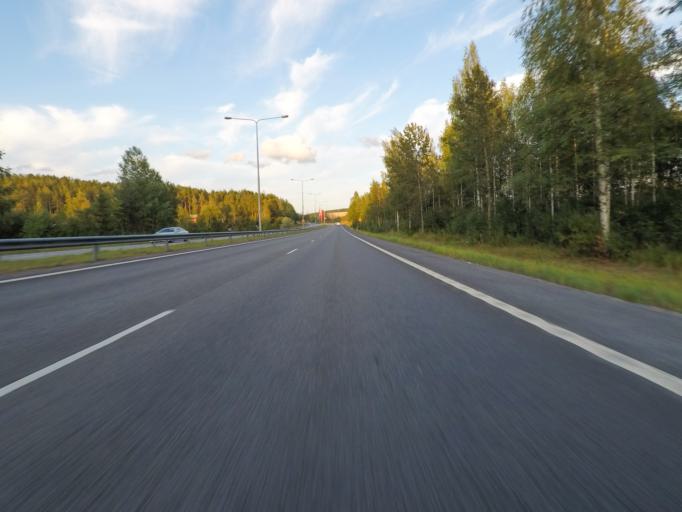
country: FI
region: Central Finland
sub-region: Jyvaeskylae
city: Saeynaetsalo
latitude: 62.2412
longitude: 25.8552
